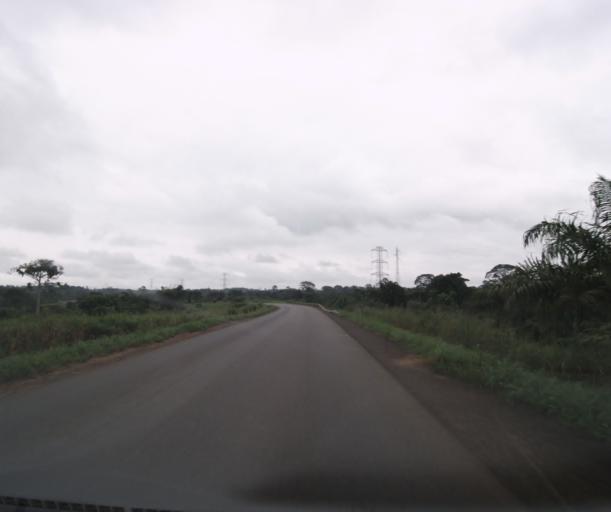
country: CM
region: Littoral
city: Edea
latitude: 3.7481
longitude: 10.1196
